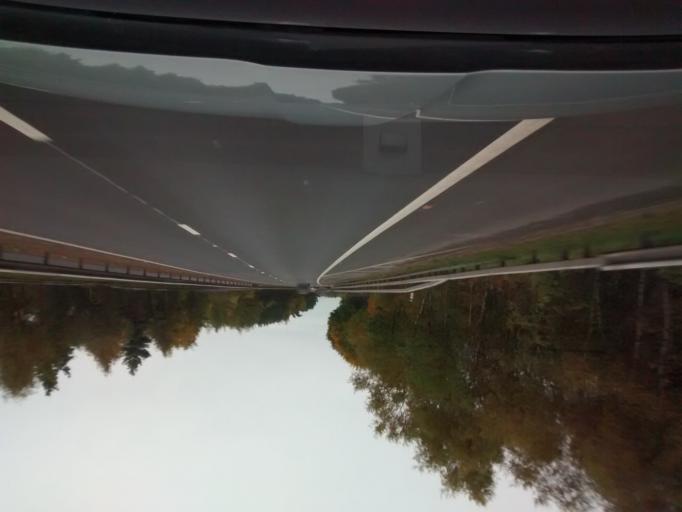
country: GB
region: Scotland
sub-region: Stirling
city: Cowie
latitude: 56.0560
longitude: -3.8486
